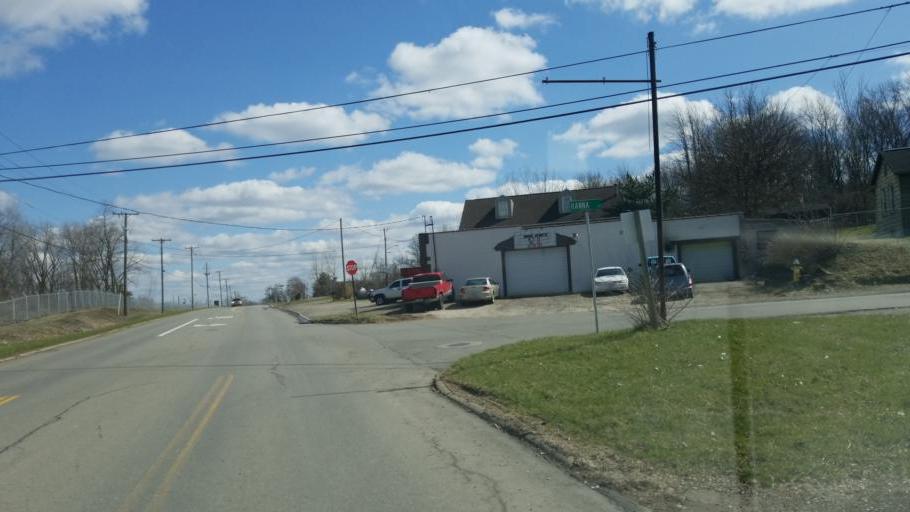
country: US
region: Ohio
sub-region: Richland County
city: Mansfield
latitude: 40.7880
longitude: -82.5266
